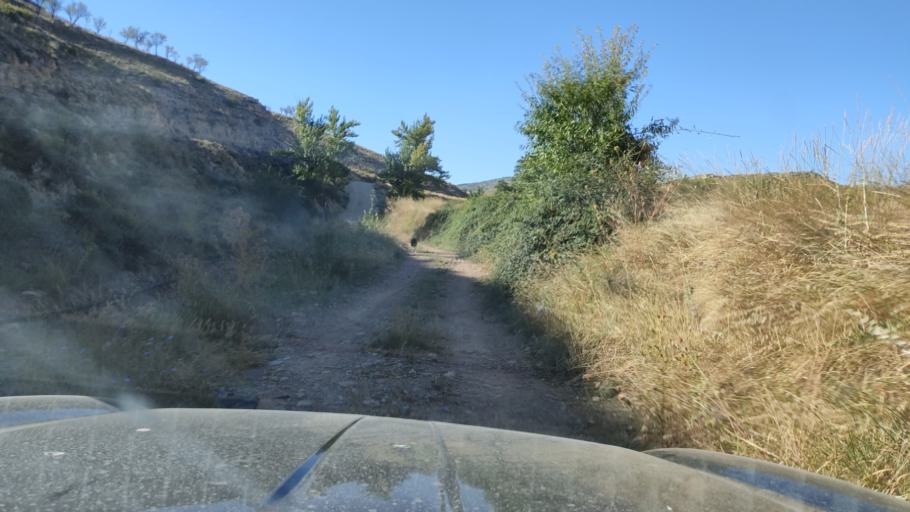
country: ES
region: Aragon
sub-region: Provincia de Teruel
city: Monforte de Moyuela
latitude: 41.0448
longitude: -1.0136
